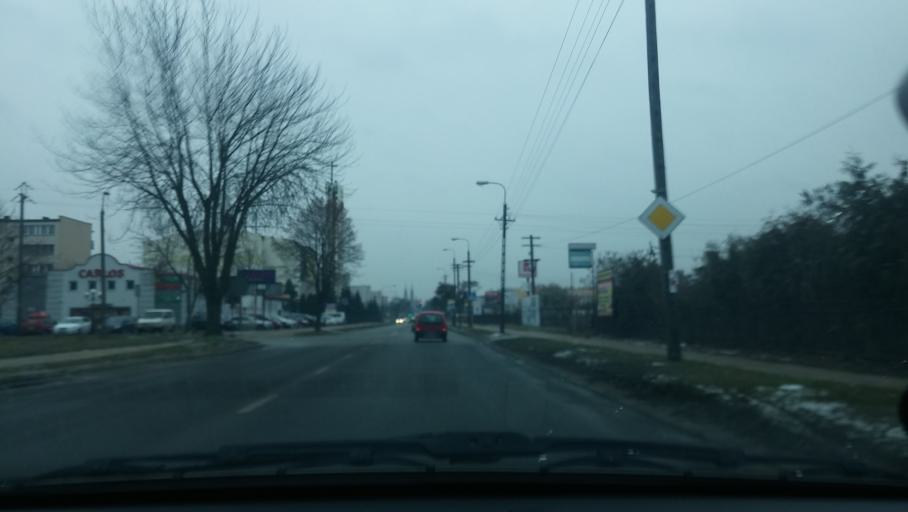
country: PL
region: Masovian Voivodeship
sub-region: Siedlce
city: Siedlce
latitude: 52.1839
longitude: 22.2684
